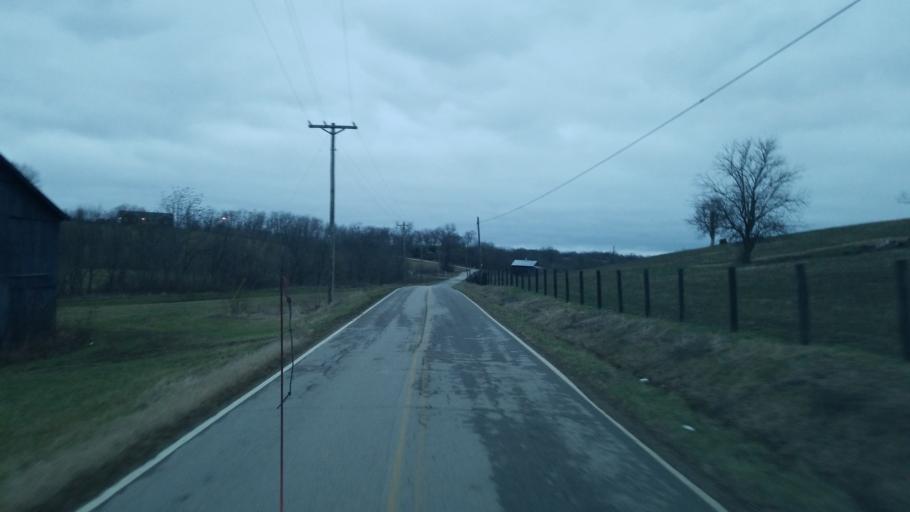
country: US
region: Kentucky
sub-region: Fleming County
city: Flemingsburg
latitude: 38.5057
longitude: -83.7013
